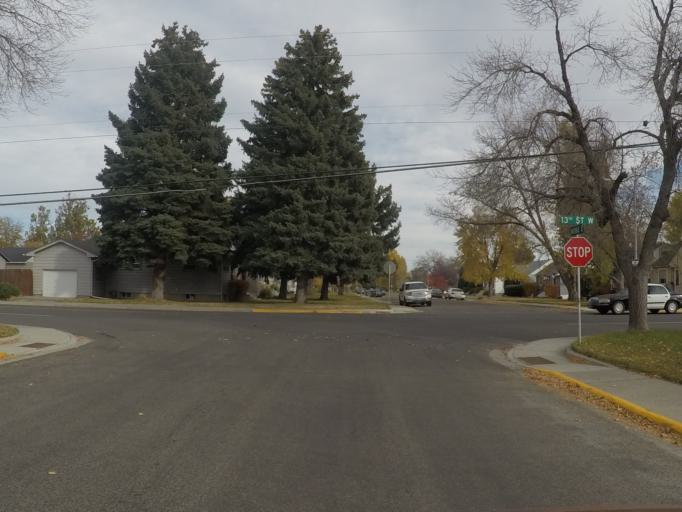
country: US
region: Montana
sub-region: Yellowstone County
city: Billings
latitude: 45.7880
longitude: -108.5489
